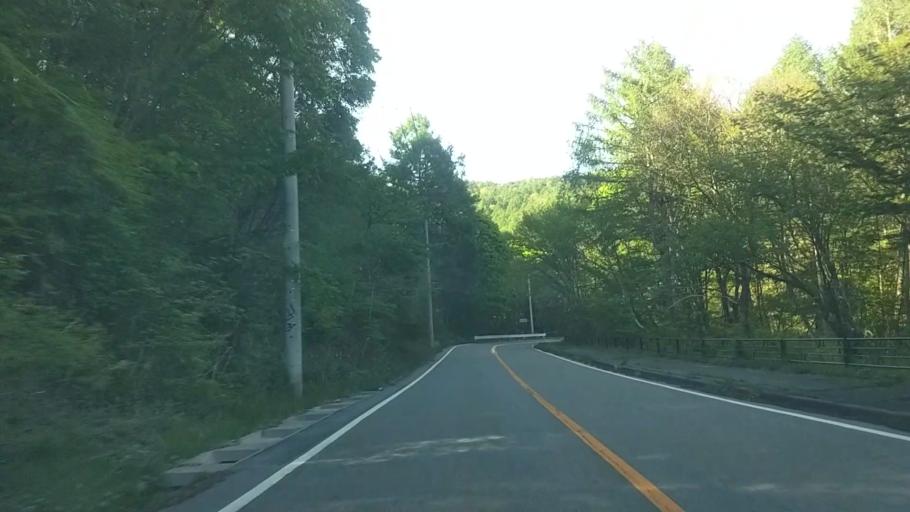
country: JP
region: Yamanashi
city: Nirasaki
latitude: 35.9067
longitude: 138.3846
